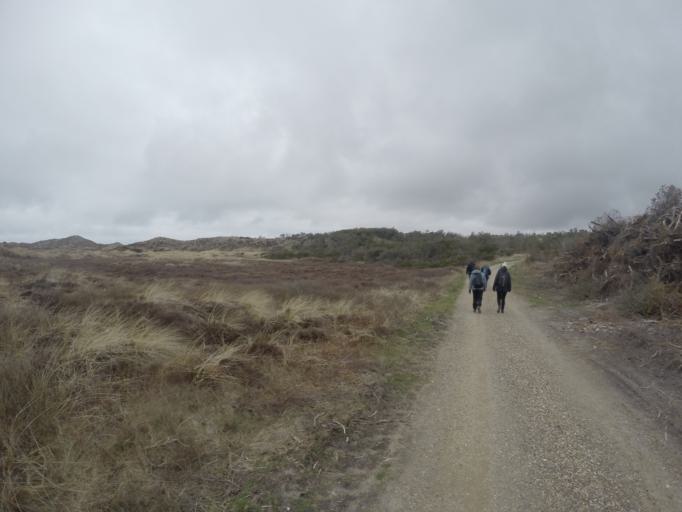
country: DK
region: North Denmark
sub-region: Thisted Kommune
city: Hurup
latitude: 56.8687
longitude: 8.3035
